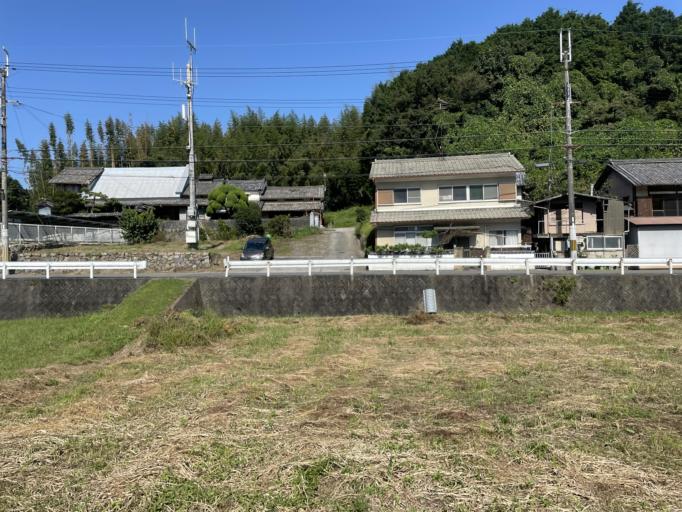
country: JP
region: Nara
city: Gose
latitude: 34.4393
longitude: 135.7686
